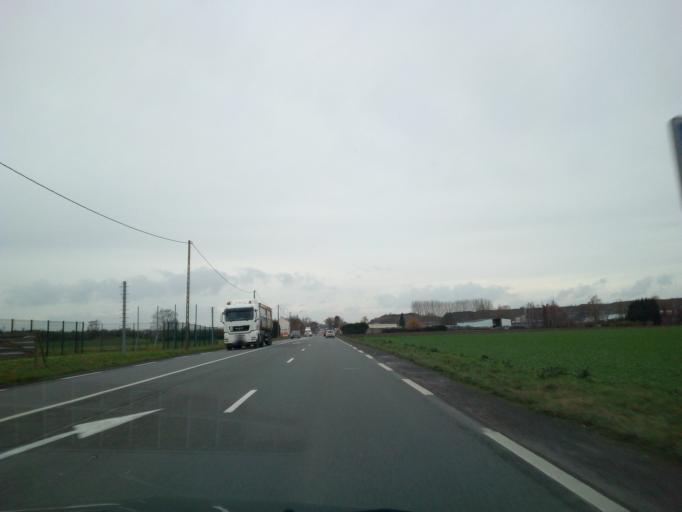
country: FR
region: Nord-Pas-de-Calais
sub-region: Departement du Pas-de-Calais
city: Annequin
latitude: 50.5105
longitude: 2.7142
